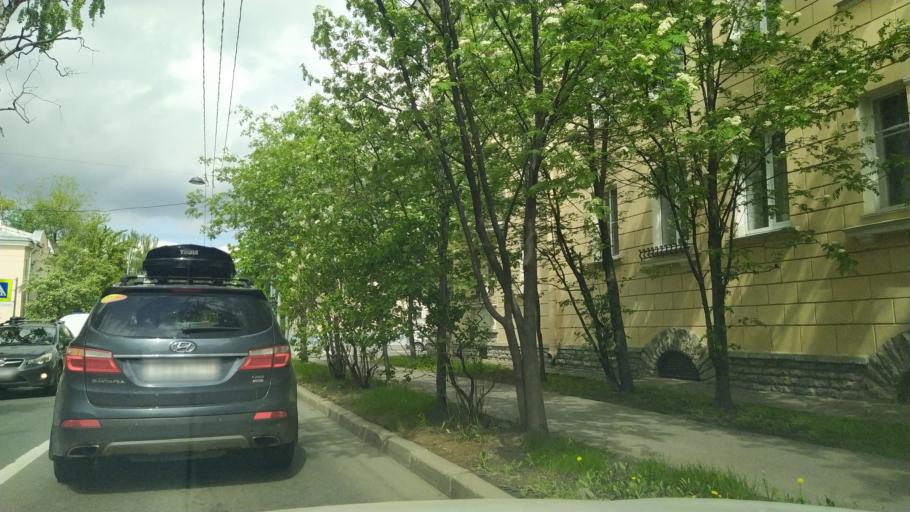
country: RU
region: St.-Petersburg
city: Novaya Derevnya
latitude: 59.9840
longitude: 30.2779
